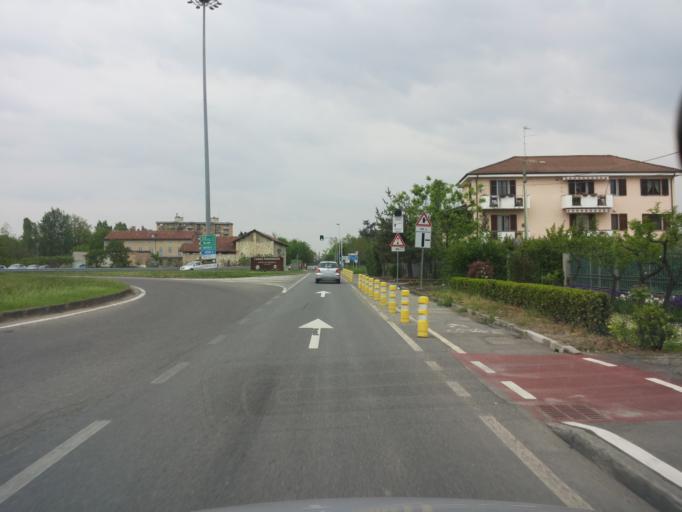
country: IT
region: Piedmont
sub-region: Provincia di Alessandria
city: Casale Monferrato
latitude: 45.1153
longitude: 8.4515
